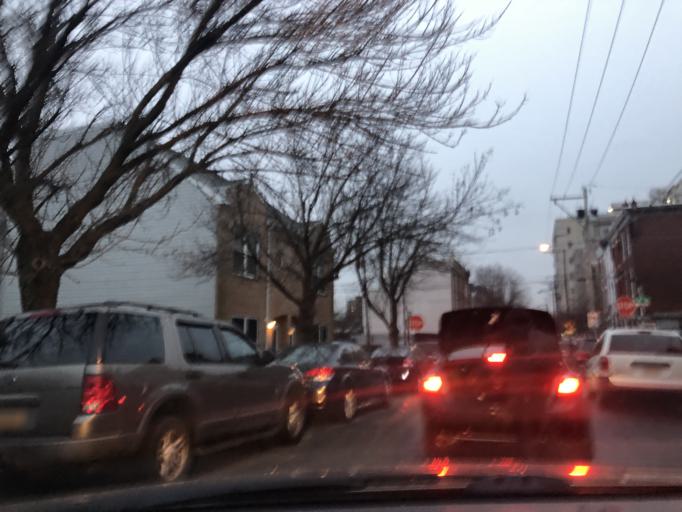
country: US
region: Pennsylvania
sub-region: Philadelphia County
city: Philadelphia
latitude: 39.9724
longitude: -75.1422
